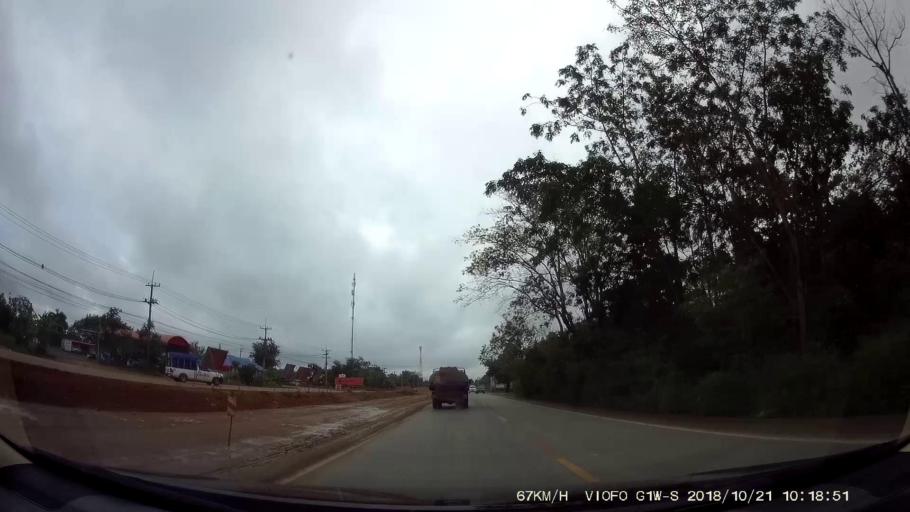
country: TH
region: Chaiyaphum
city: Phu Khiao
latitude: 16.3189
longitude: 102.1951
